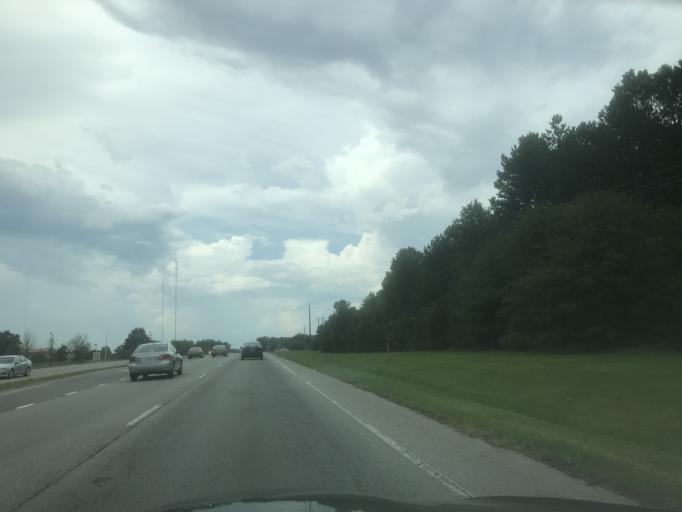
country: US
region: North Carolina
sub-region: Johnston County
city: Clayton
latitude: 35.6630
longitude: -78.4918
